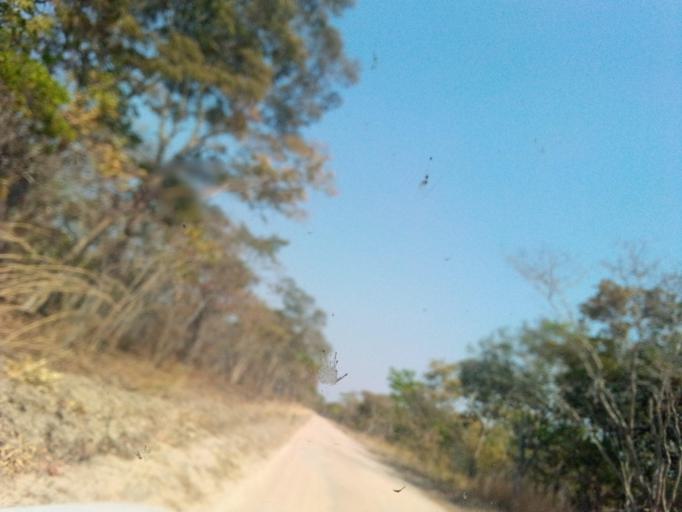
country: ZM
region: Northern
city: Mpika
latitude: -12.2256
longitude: 30.8999
